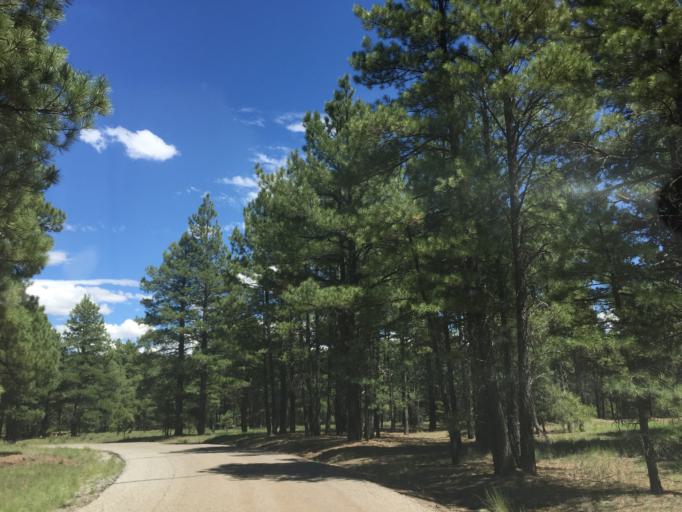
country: US
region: Arizona
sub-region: Coconino County
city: Mountainaire
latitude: 35.0258
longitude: -111.4567
